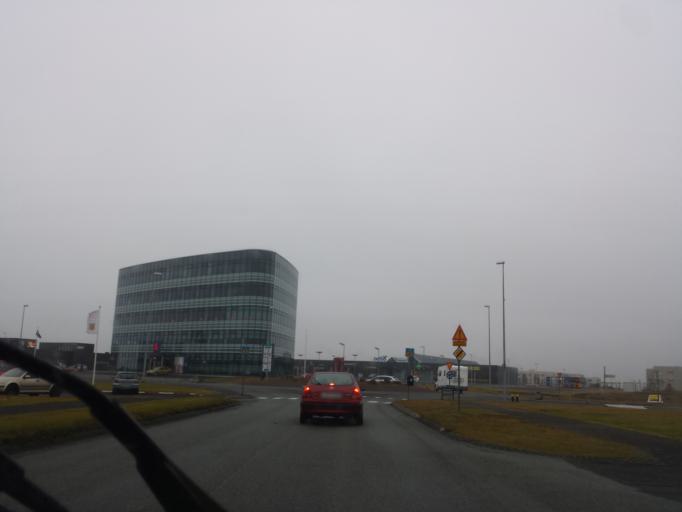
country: IS
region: Southern Peninsula
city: Reykjanesbaer
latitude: 63.9956
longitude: -22.5527
